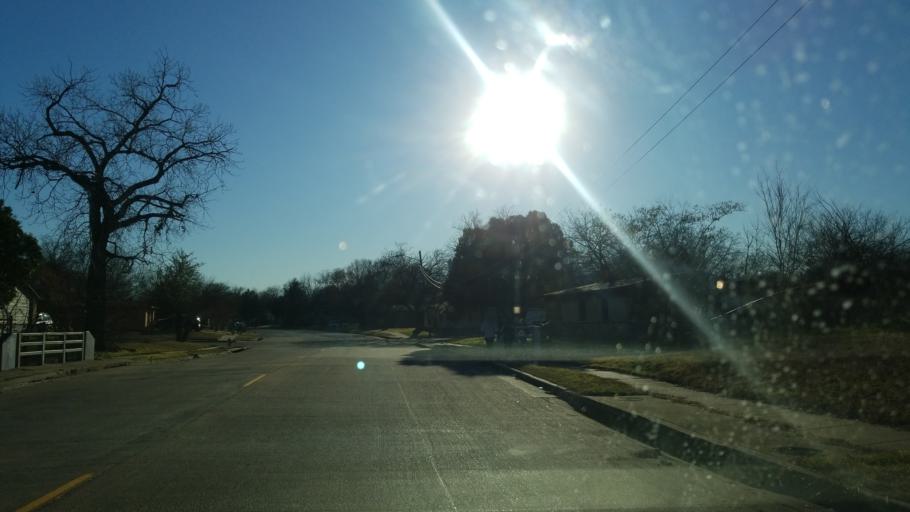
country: US
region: Texas
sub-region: Tarrant County
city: Arlington
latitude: 32.7315
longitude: -97.0666
